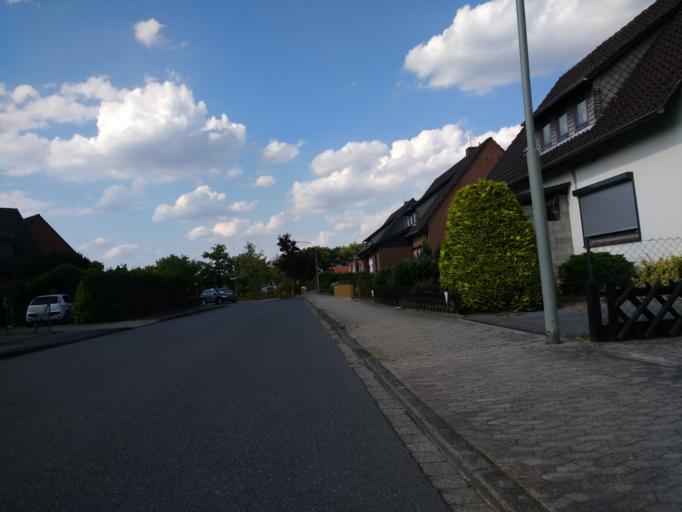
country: DE
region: Lower Saxony
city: Wagenhoff
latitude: 52.4980
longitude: 10.5134
